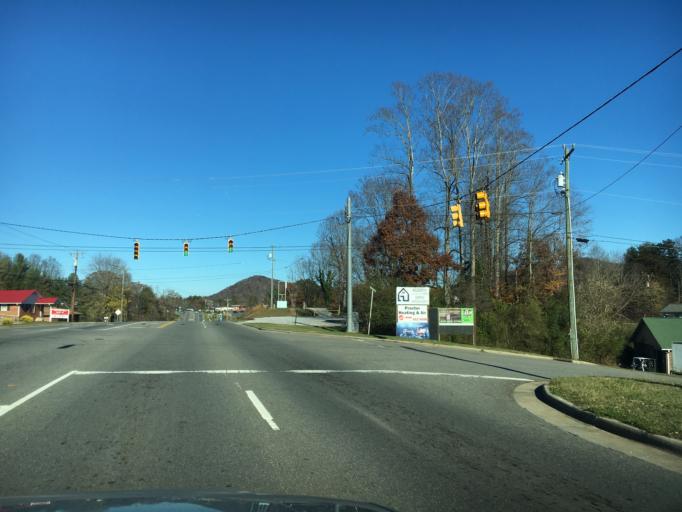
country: US
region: North Carolina
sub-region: McDowell County
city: West Marion
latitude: 35.6529
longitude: -82.0309
